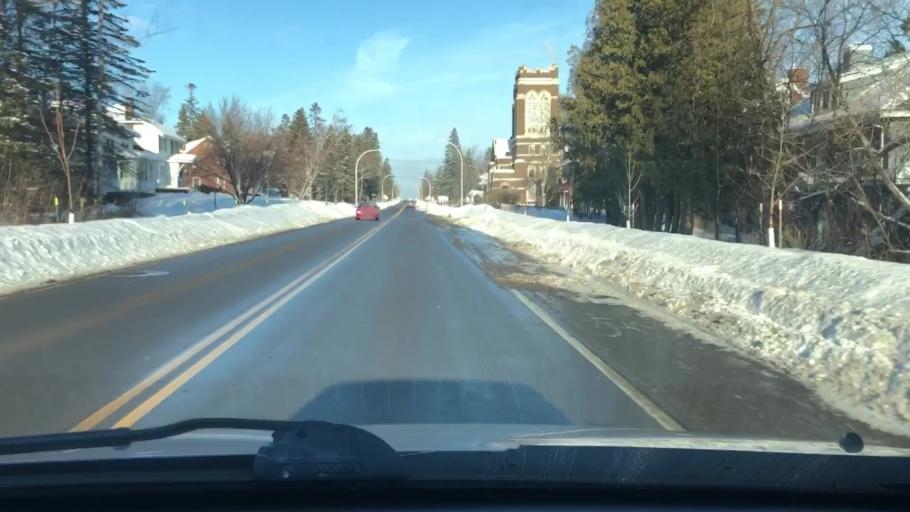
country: US
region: Minnesota
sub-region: Saint Louis County
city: Duluth
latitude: 46.8108
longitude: -92.0749
